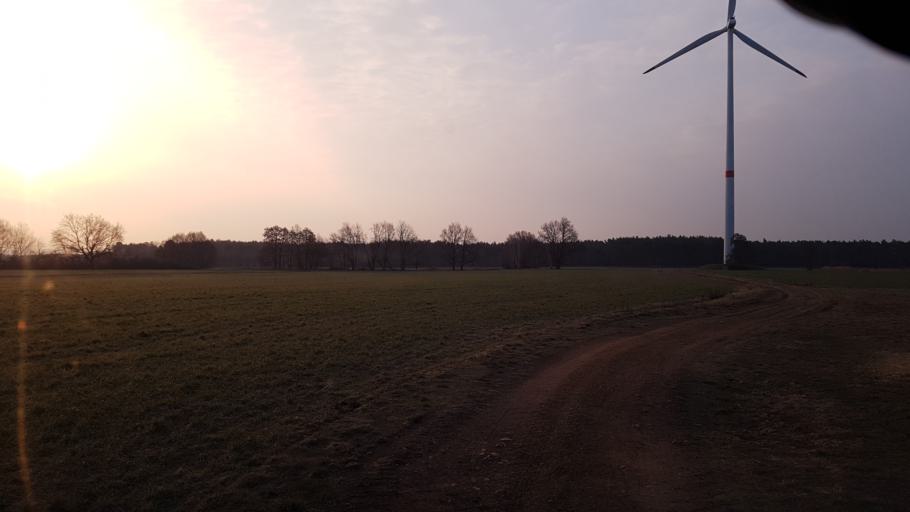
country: DE
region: Brandenburg
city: Falkenberg
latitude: 51.5714
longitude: 13.3025
